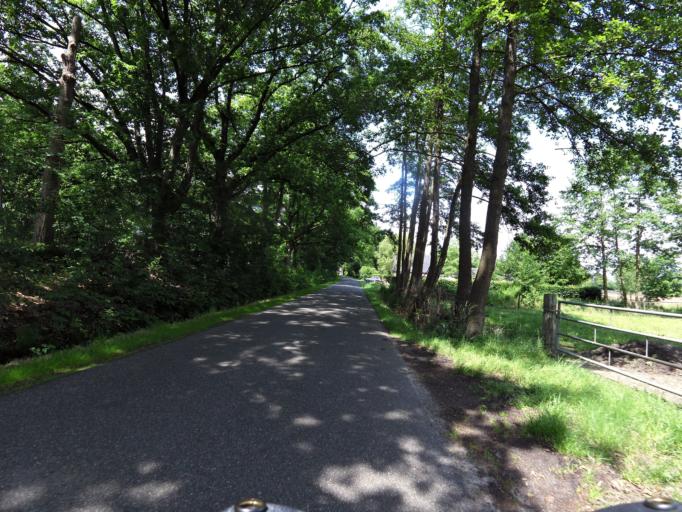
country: NL
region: Gelderland
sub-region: Gemeente Apeldoorn
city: Loenen
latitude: 52.1505
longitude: 6.0367
